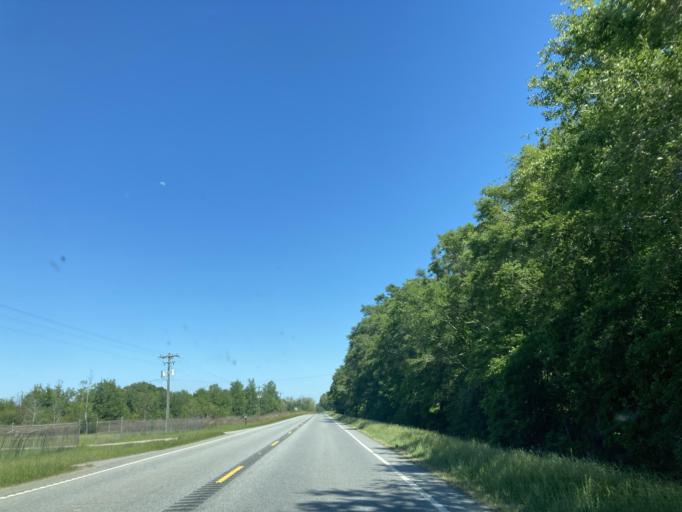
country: US
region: Georgia
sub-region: Miller County
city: Colquitt
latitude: 31.1837
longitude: -84.5542
